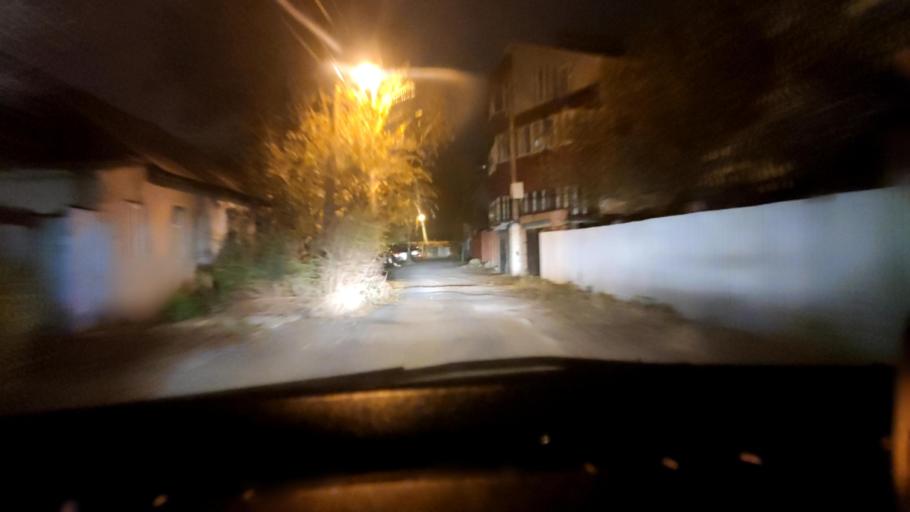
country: RU
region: Voronezj
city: Voronezh
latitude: 51.6476
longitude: 39.1713
